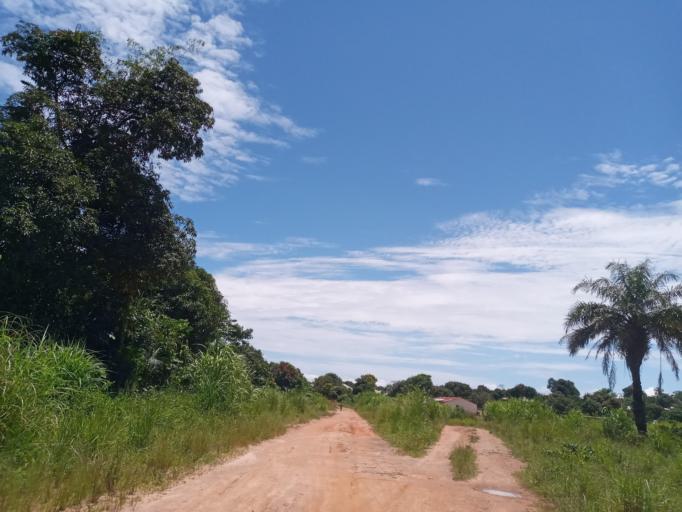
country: SL
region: Eastern Province
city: Koidu
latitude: 8.6516
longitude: -10.9538
